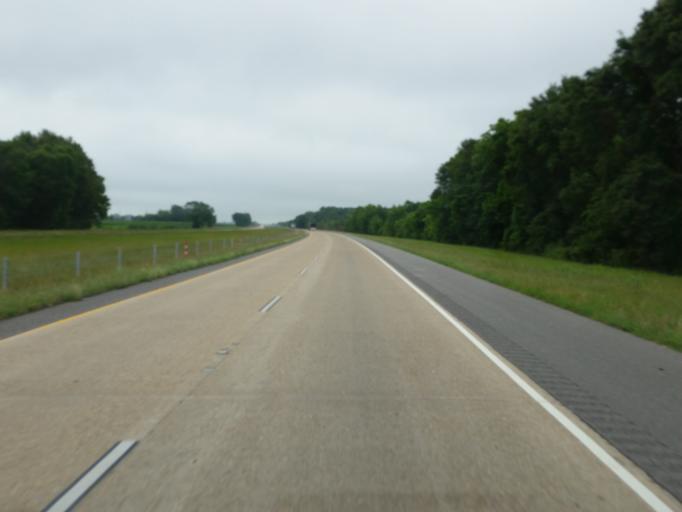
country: US
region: Louisiana
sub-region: Madison Parish
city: Tallulah
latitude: 32.3358
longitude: -91.0600
